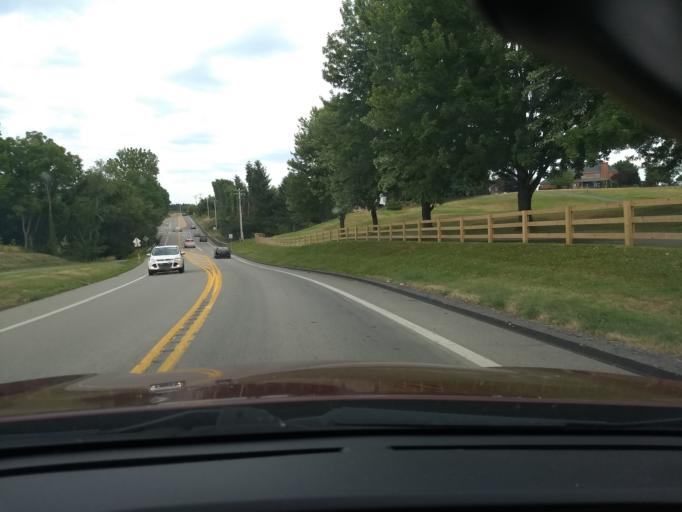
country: US
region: Pennsylvania
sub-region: Butler County
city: Mars
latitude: 40.6679
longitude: -80.0273
